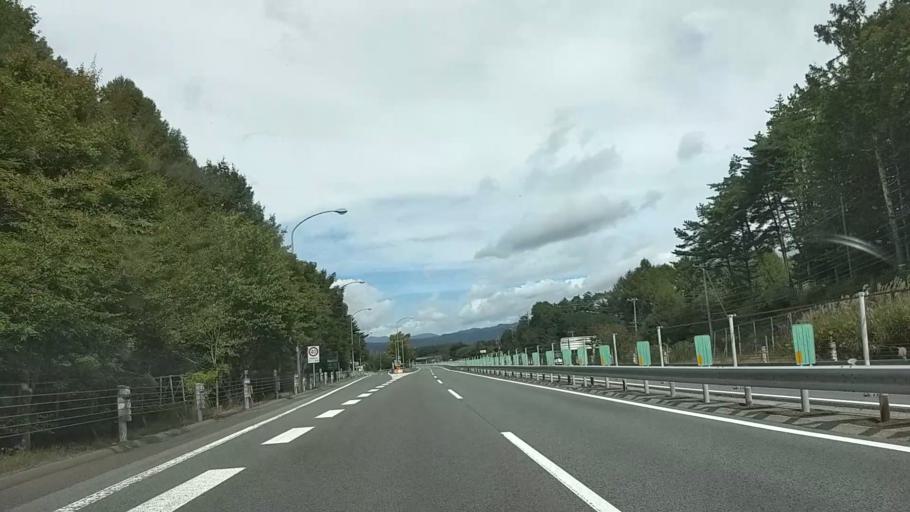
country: JP
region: Nagano
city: Chino
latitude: 35.9522
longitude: 138.1990
